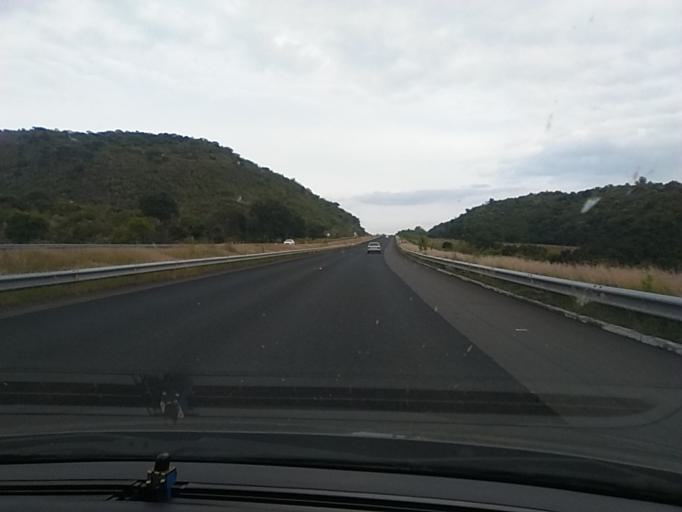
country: MX
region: Mexico
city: Huaniqueo de Morales
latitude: 19.8867
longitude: -101.4578
